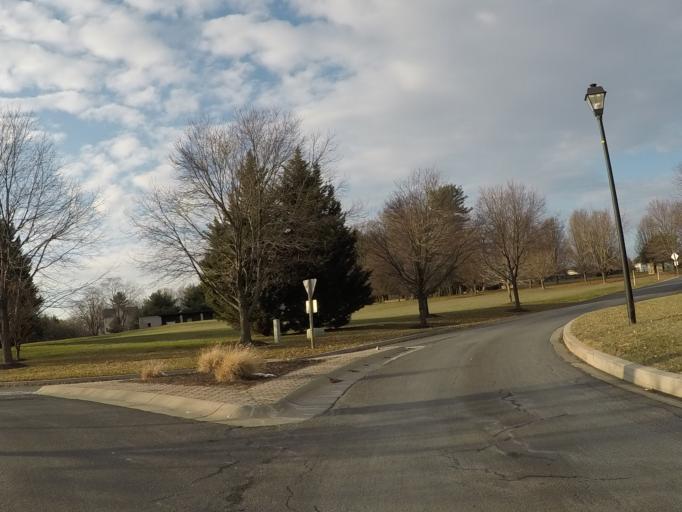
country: US
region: Maryland
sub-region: Howard County
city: Columbia
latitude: 39.2854
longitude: -76.9036
